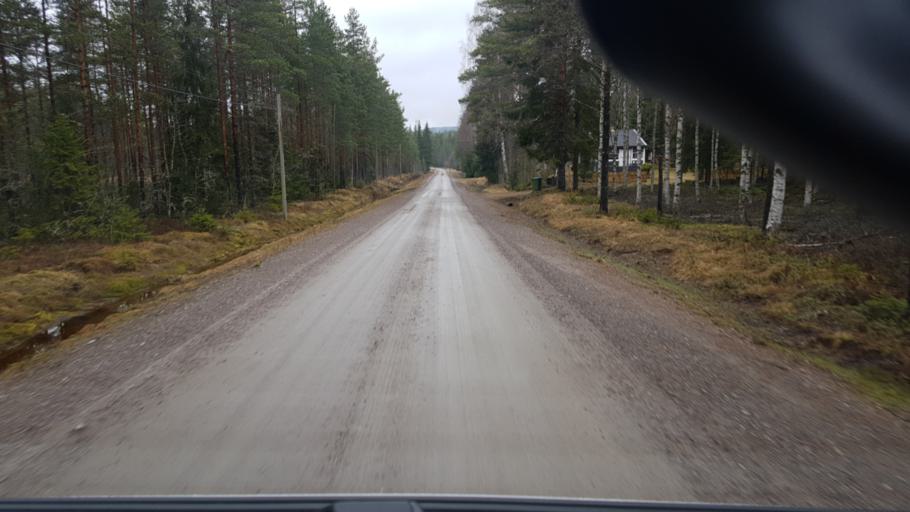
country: SE
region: Vaermland
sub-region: Eda Kommun
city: Charlottenberg
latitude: 59.9661
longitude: 12.5052
